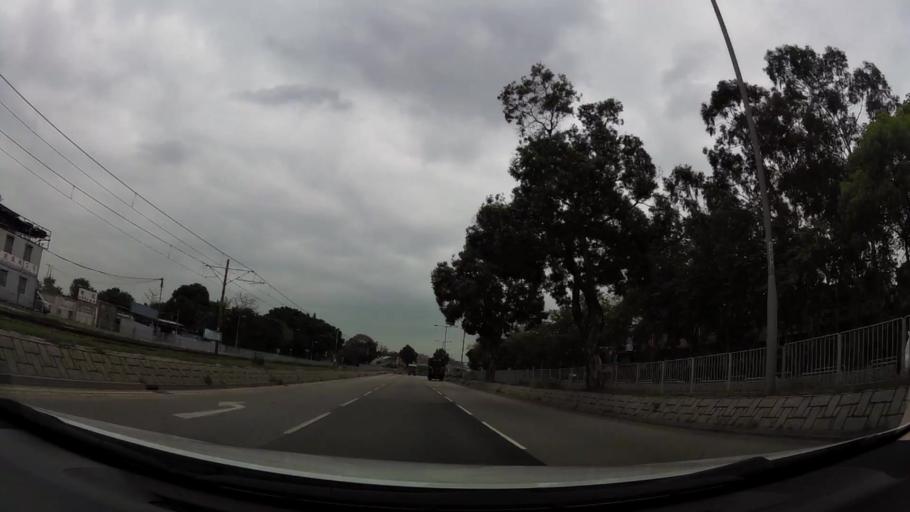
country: HK
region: Tuen Mun
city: Tuen Mun
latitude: 22.4283
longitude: 113.9908
